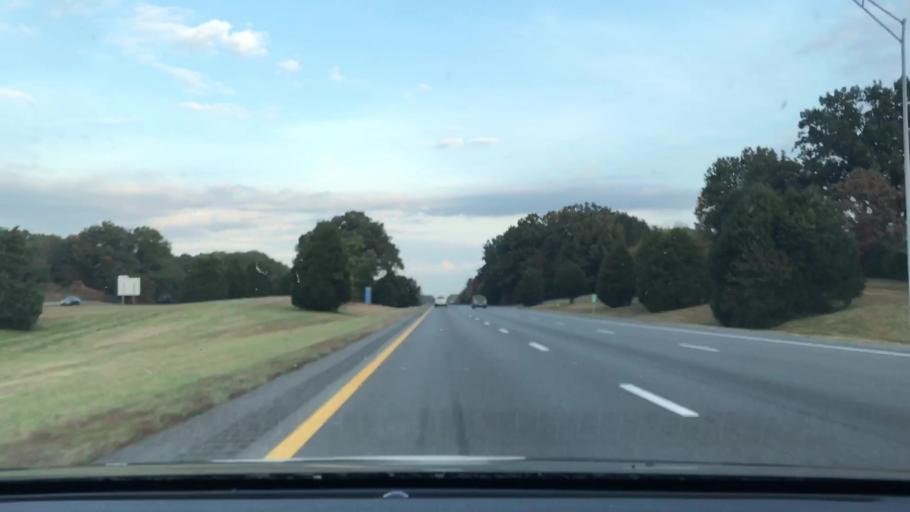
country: US
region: Tennessee
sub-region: Montgomery County
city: Clarksville
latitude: 36.6041
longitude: -87.2859
